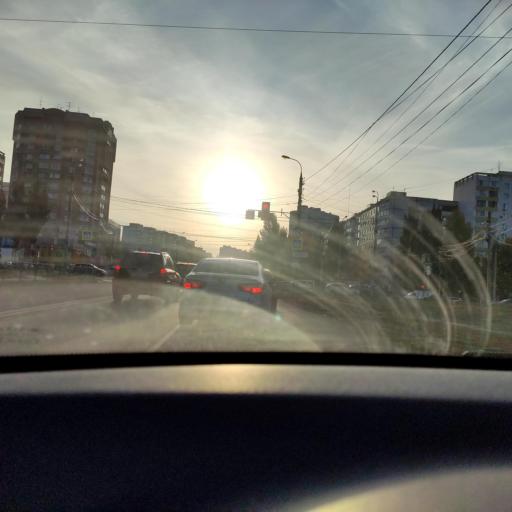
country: RU
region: Samara
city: Samara
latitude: 53.2646
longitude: 50.2173
